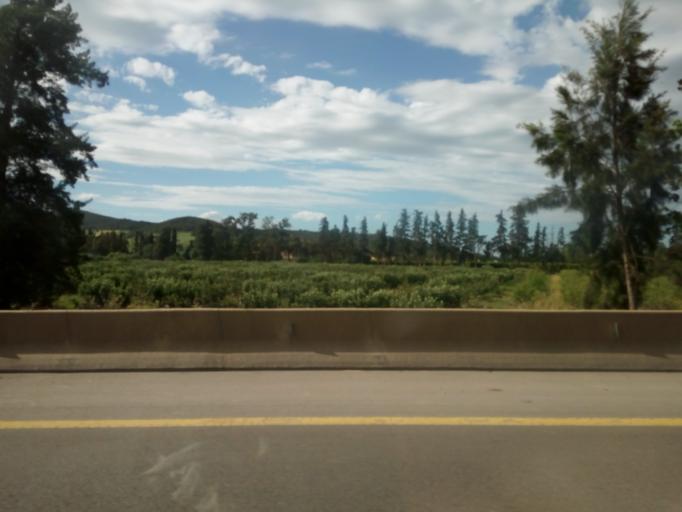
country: DZ
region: Tipaza
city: El Affroun
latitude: 36.4463
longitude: 2.5896
